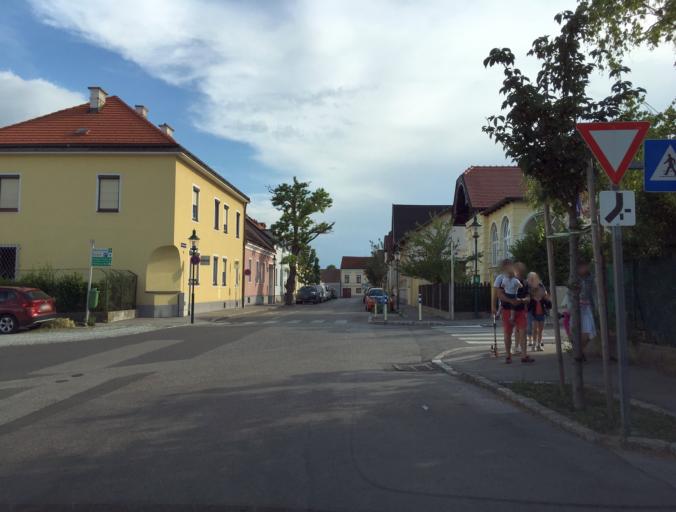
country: AT
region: Lower Austria
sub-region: Politischer Bezirk Modling
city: Gumpoldskirchen
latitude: 48.0443
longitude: 16.2834
